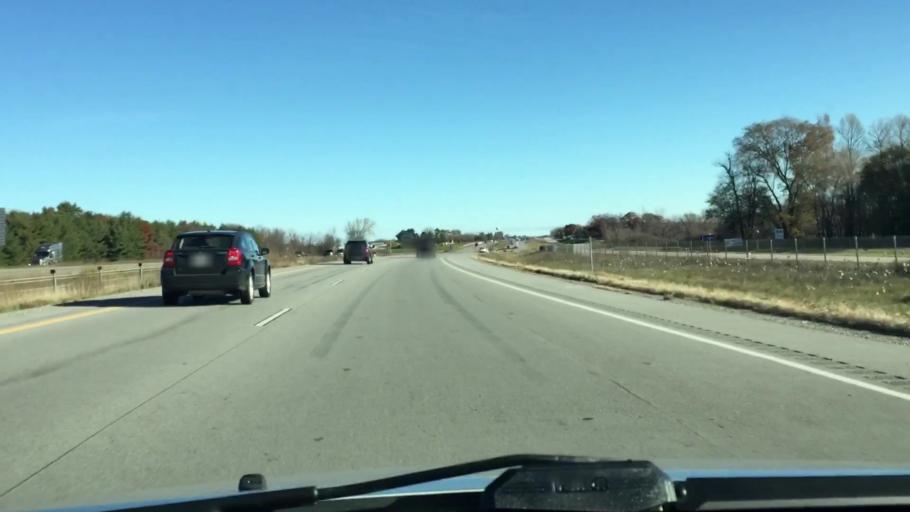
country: US
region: Wisconsin
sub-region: Brown County
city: Wrightstown
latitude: 44.3913
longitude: -88.1593
